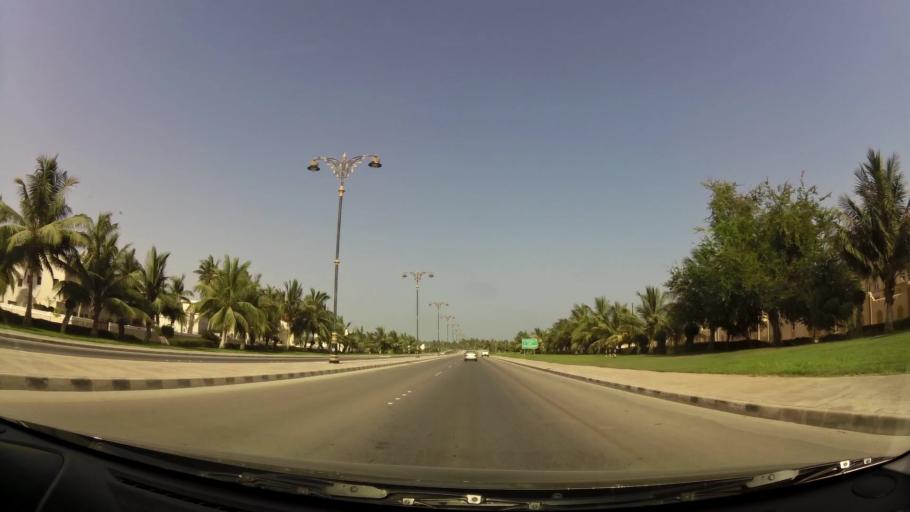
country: OM
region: Zufar
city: Salalah
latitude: 17.0031
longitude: 54.0634
